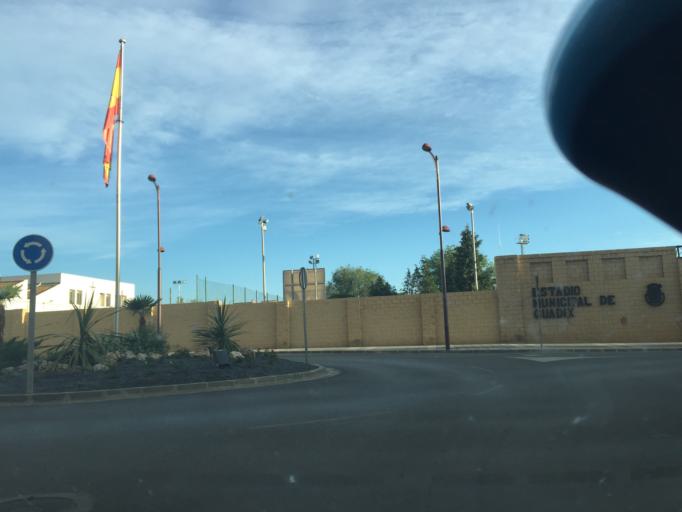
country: ES
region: Andalusia
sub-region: Provincia de Granada
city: Guadix
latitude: 37.3063
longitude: -3.1413
